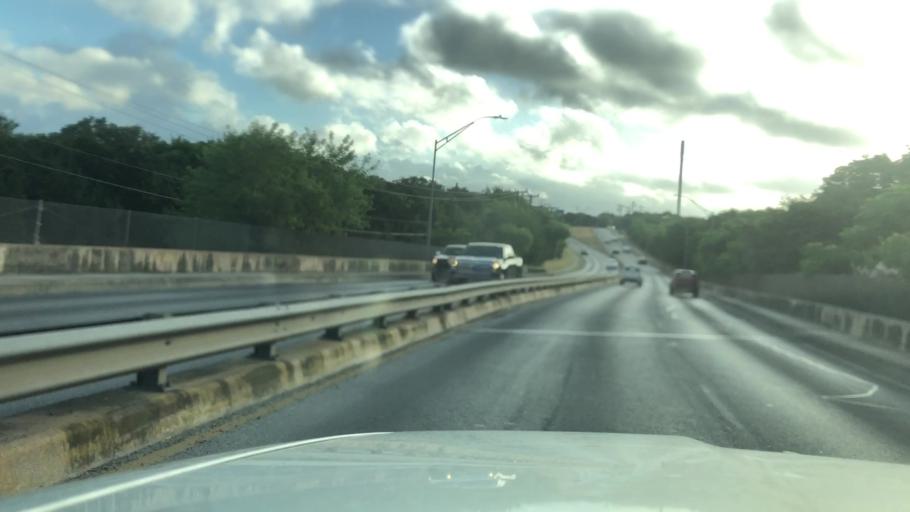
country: US
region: Texas
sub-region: Bexar County
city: Shavano Park
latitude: 29.5694
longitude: -98.5529
